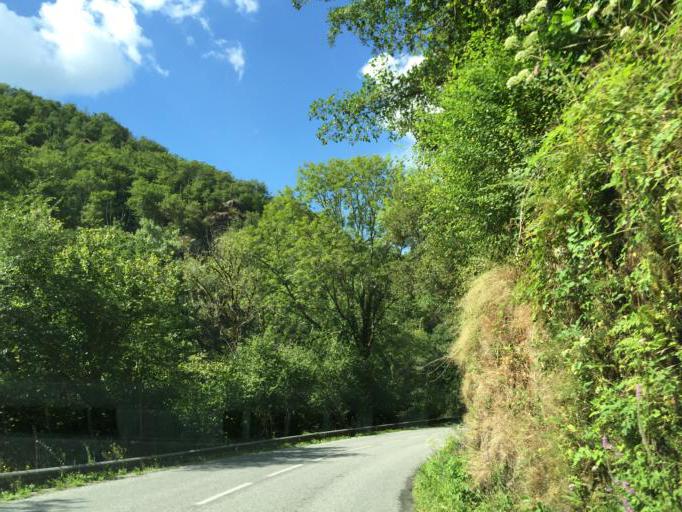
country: FR
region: Midi-Pyrenees
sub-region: Departement de l'Aveyron
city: Saint-Christophe-Vallon
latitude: 44.5749
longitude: 2.4071
